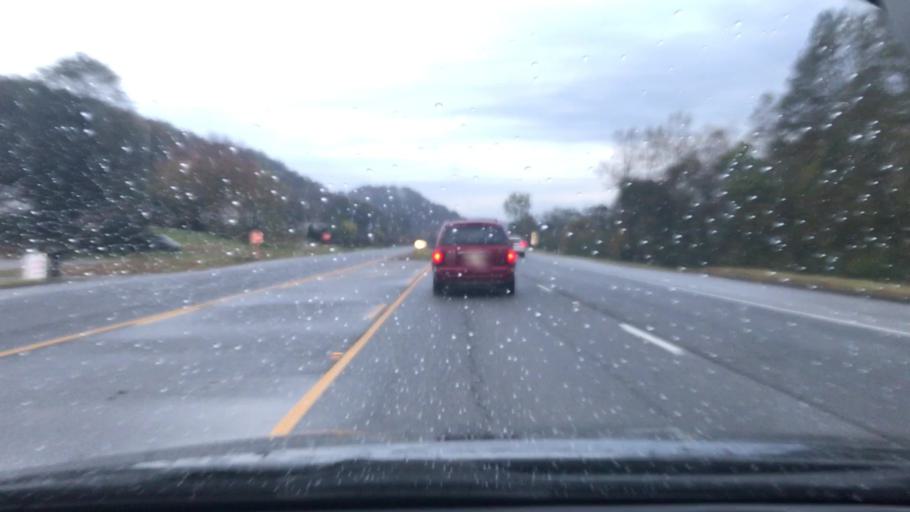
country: US
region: Tennessee
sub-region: Cheatham County
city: Ashland City
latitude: 36.2583
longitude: -87.0431
